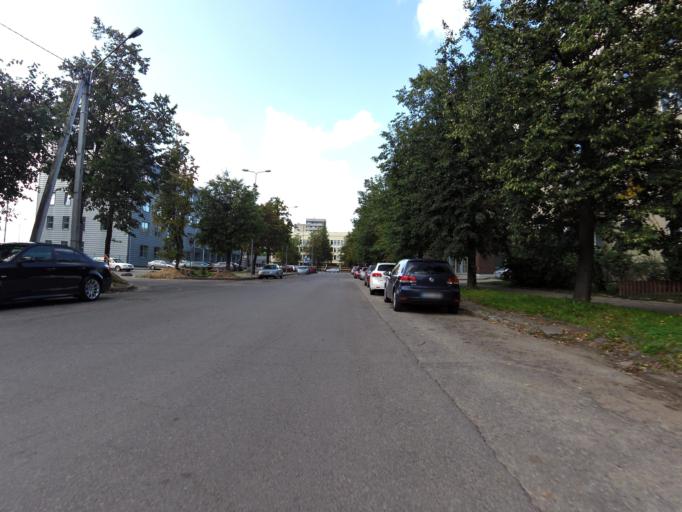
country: LT
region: Vilnius County
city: Naujamiestis
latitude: 54.6757
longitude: 25.2614
